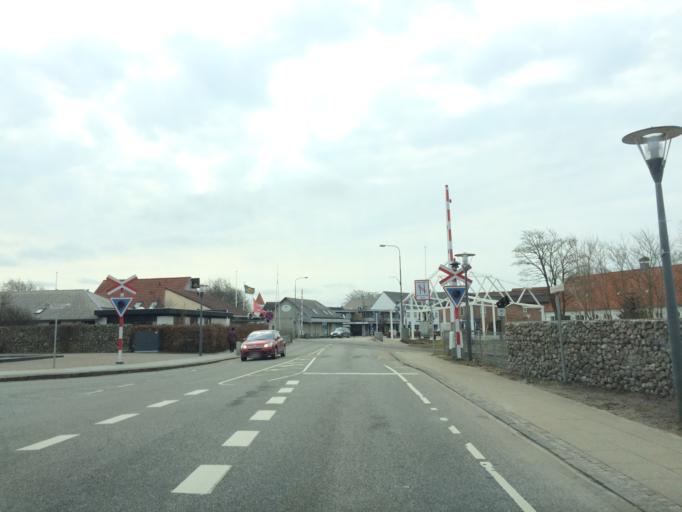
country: DK
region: Central Jutland
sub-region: Ringkobing-Skjern Kommune
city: Tarm
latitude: 55.9097
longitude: 8.5212
